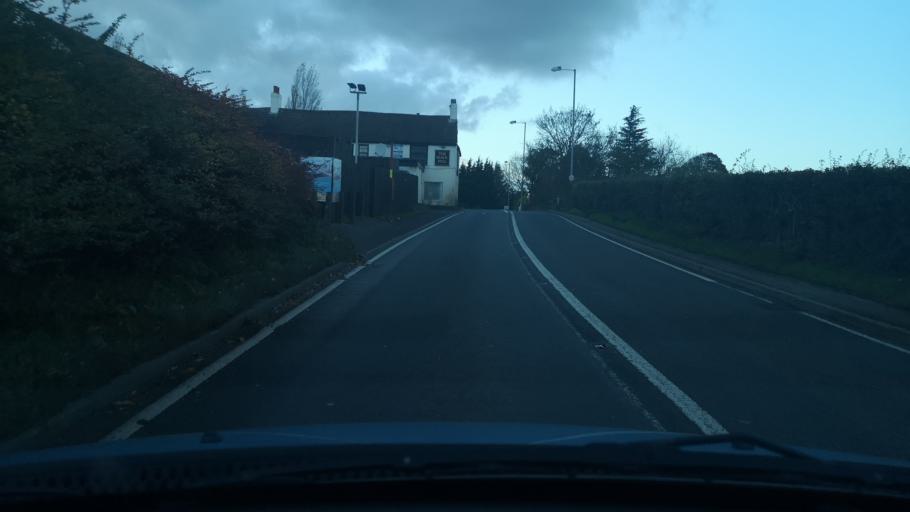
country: GB
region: England
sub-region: City and Borough of Wakefield
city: Middlestown
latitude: 53.6276
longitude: -1.5893
